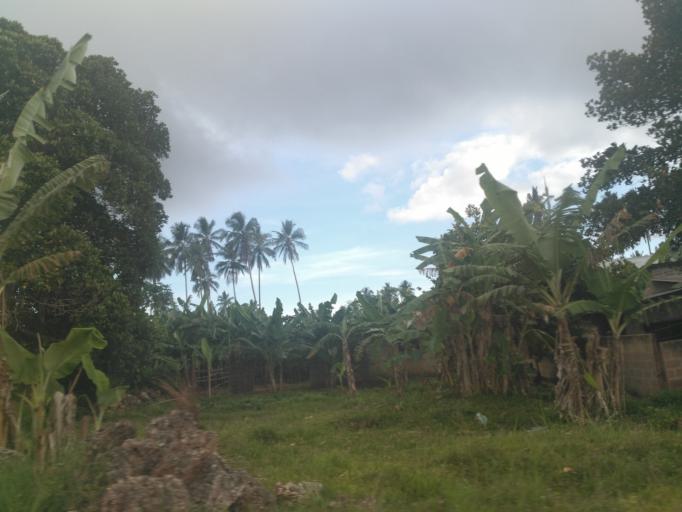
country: TZ
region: Zanzibar Central/South
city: Koani
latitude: -6.1057
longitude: 39.2863
